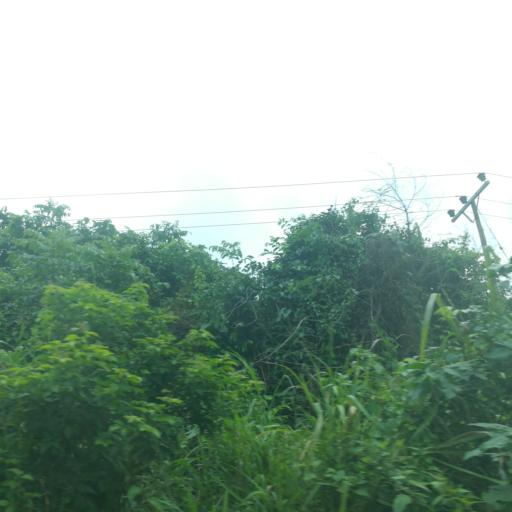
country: NG
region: Ogun
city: Odogbolu
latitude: 6.6679
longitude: 3.7101
